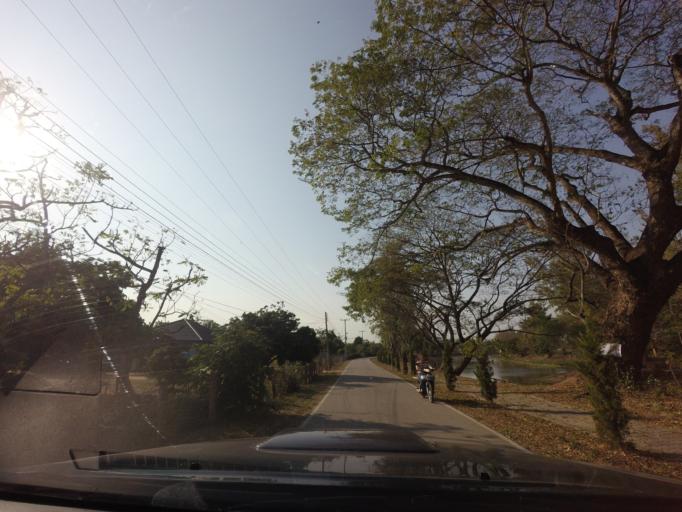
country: TH
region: Chiang Mai
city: San Sai
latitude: 18.9354
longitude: 98.9718
